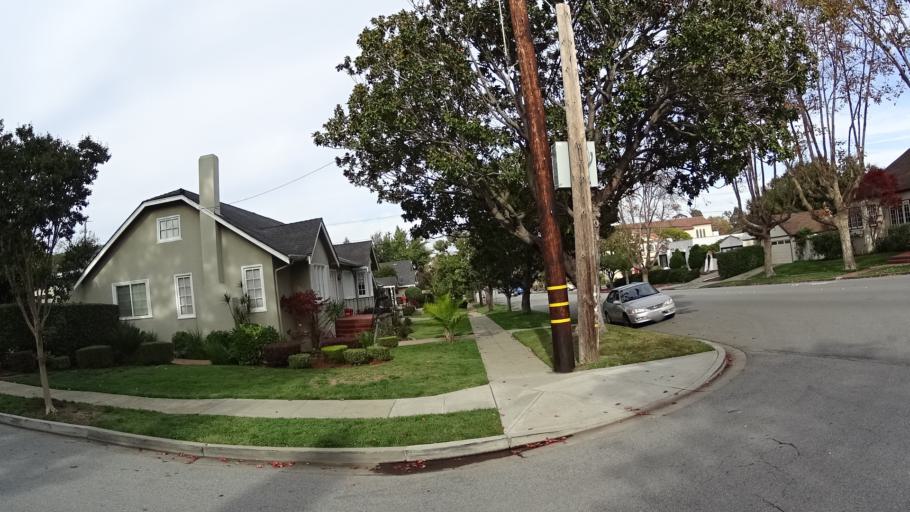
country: US
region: California
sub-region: San Mateo County
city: Burlingame
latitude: 37.5847
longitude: -122.3745
